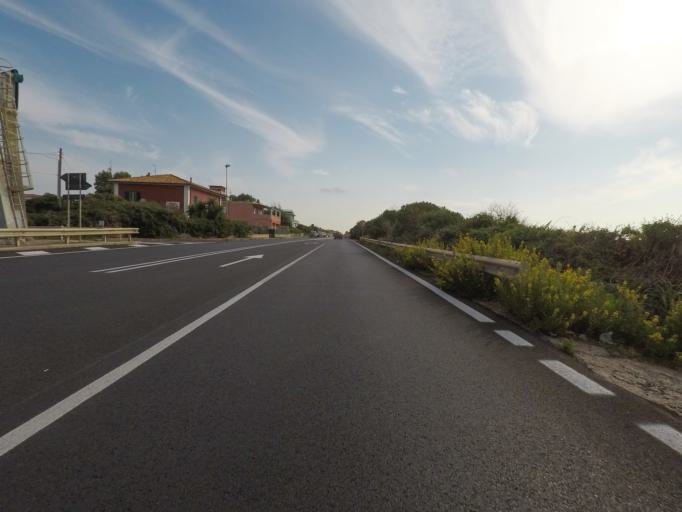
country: IT
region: Latium
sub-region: Citta metropolitana di Roma Capitale
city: Civitavecchia
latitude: 42.0553
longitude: 11.8199
